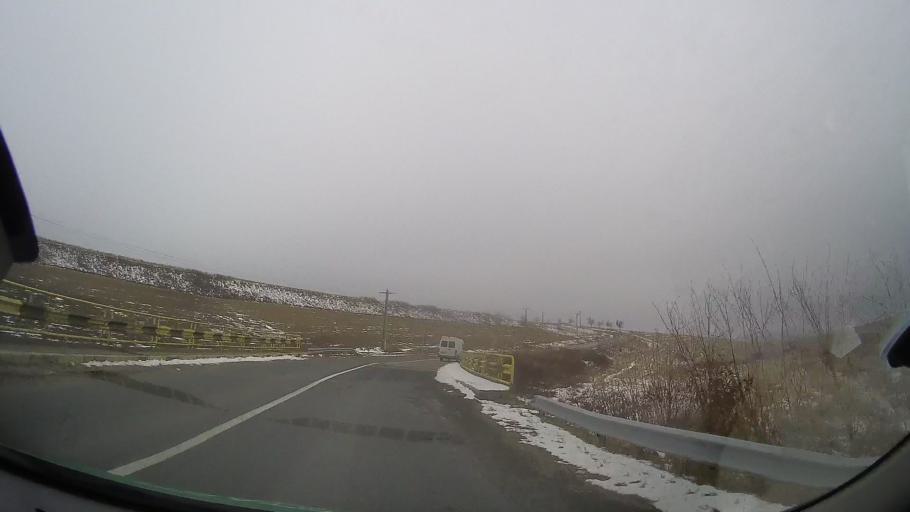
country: RO
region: Vaslui
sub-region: Comuna Grivita
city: Grivita
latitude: 46.1969
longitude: 27.6070
